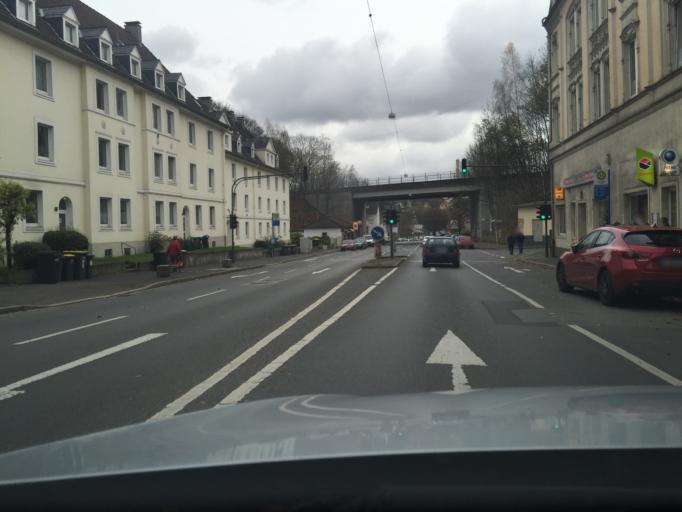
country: DE
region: North Rhine-Westphalia
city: Wulfrath
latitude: 51.2552
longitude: 7.0990
